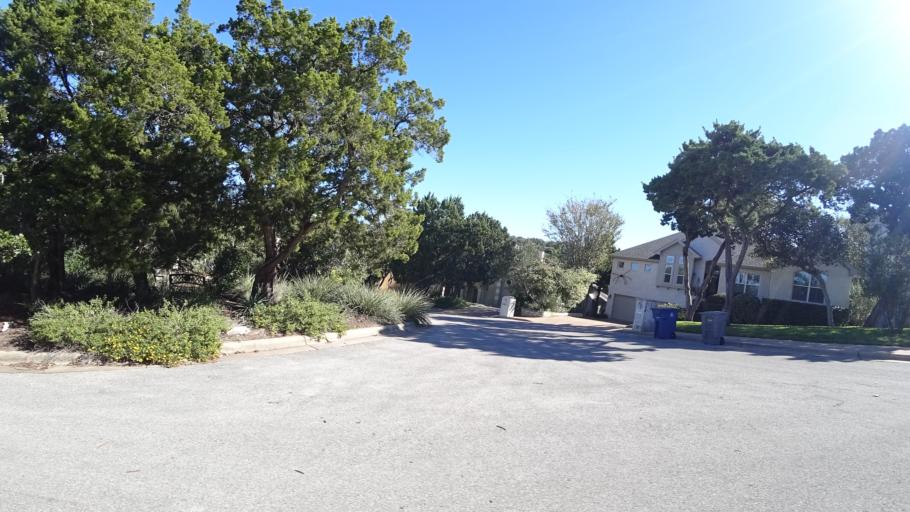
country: US
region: Texas
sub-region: Travis County
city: West Lake Hills
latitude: 30.3618
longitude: -97.7750
